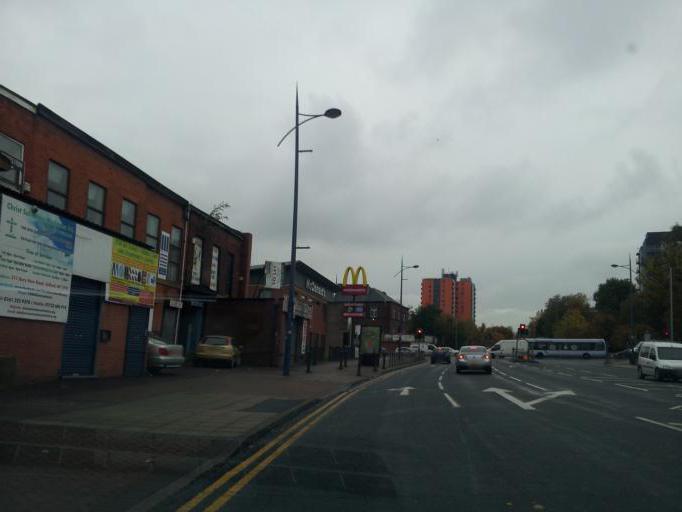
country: GB
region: England
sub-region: Manchester
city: Cheetham Hill
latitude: 53.5013
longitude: -2.2574
